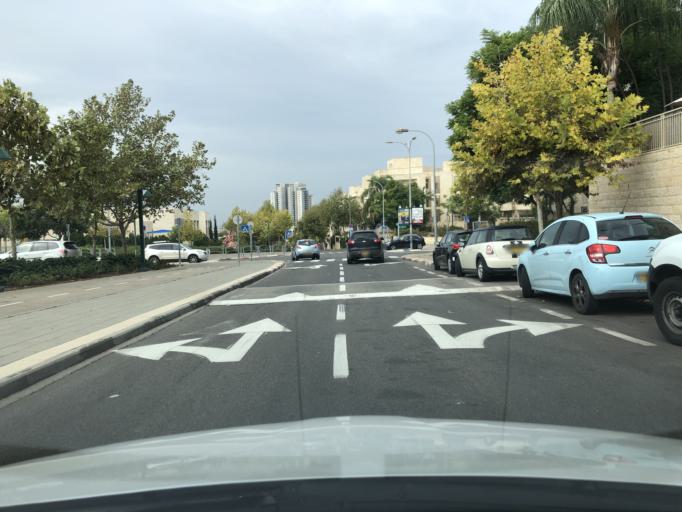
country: IL
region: Central District
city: Modiin
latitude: 31.9128
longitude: 35.0107
